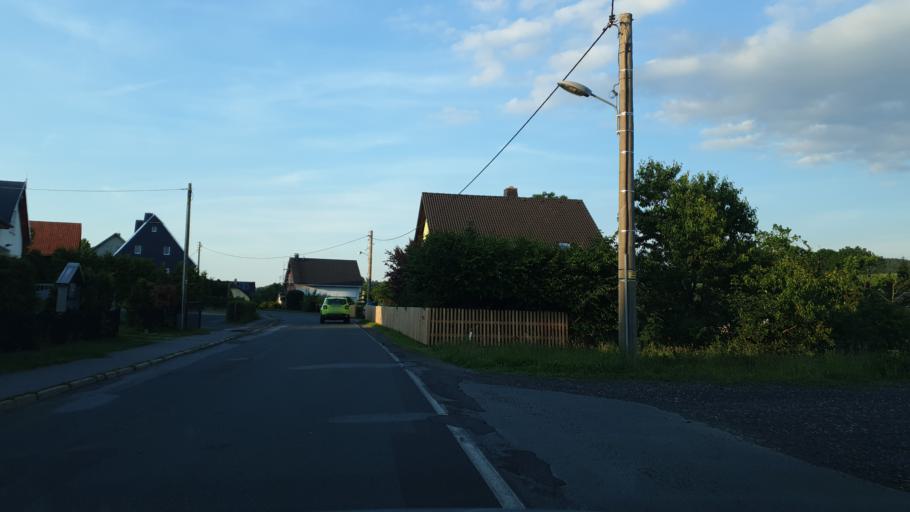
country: DE
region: Saxony
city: Stollberg
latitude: 50.6920
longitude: 12.7625
